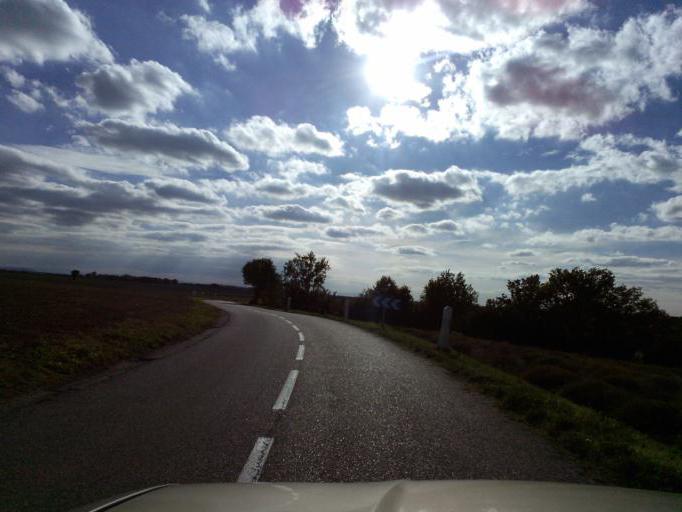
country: FR
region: Provence-Alpes-Cote d'Azur
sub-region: Departement des Alpes-de-Haute-Provence
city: Riez
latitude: 43.8929
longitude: 6.0697
